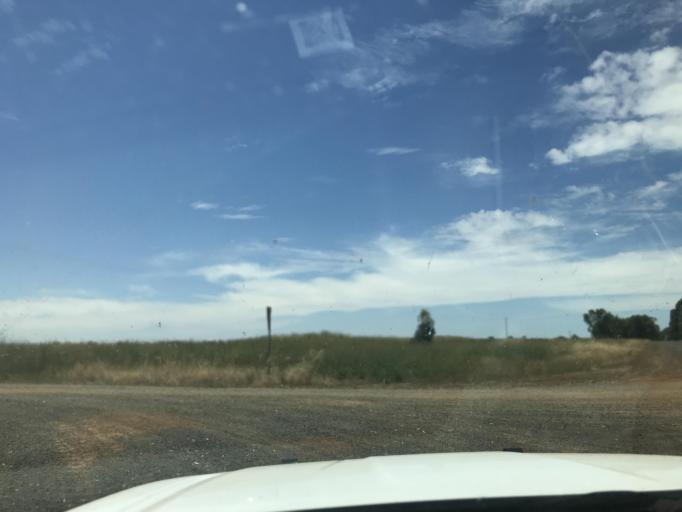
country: AU
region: Victoria
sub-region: Horsham
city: Horsham
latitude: -36.9790
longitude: 141.5308
